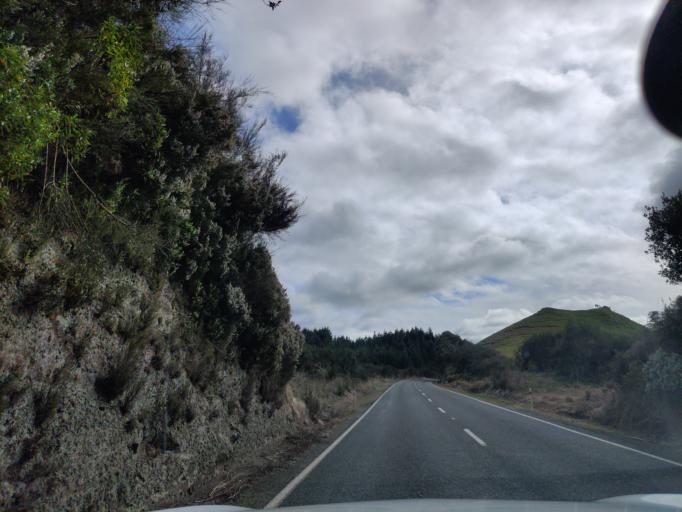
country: NZ
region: Waikato
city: Turangi
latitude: -38.7245
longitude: 175.6581
